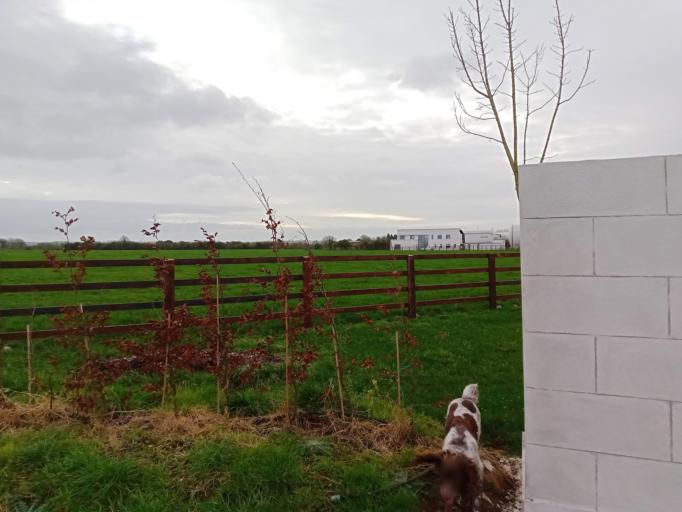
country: IE
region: Munster
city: Thurles
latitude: 52.6117
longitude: -7.7649
